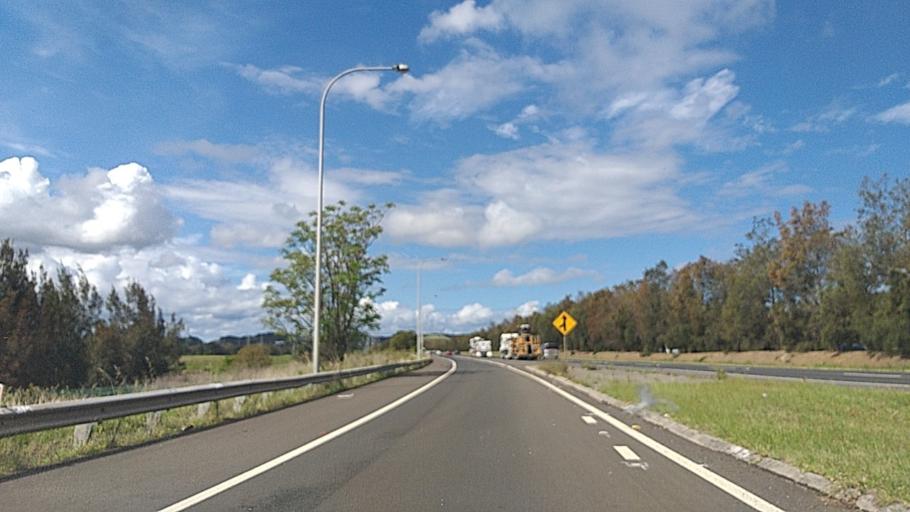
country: AU
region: New South Wales
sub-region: Wollongong
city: Koonawarra
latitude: -34.4862
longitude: 150.8113
